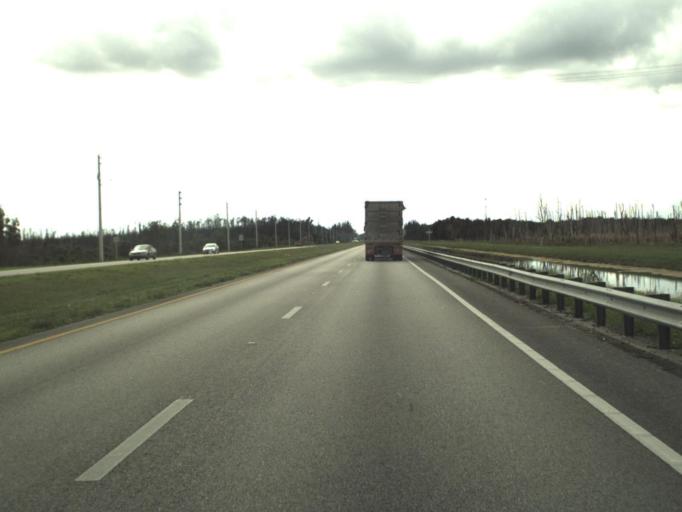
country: US
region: Florida
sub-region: Miami-Dade County
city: Tamiami
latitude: 25.7611
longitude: -80.4497
